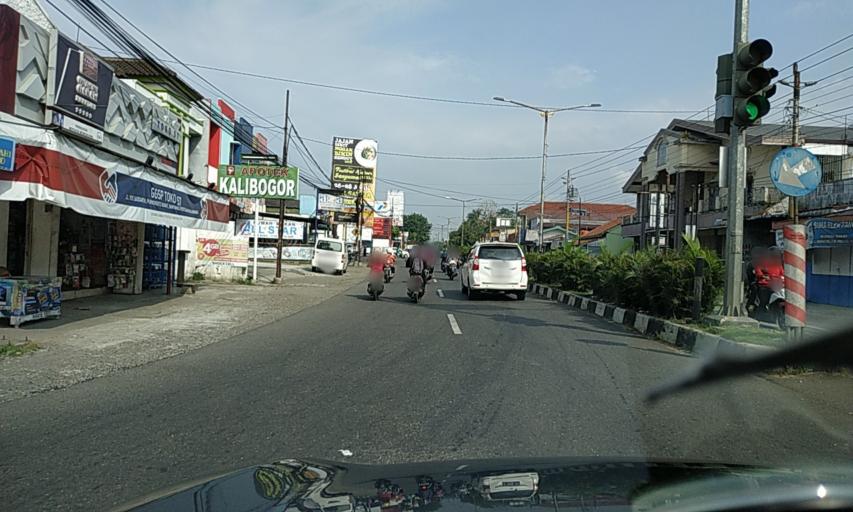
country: ID
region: Central Java
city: Purwokerto
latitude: -7.4223
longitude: 109.2126
